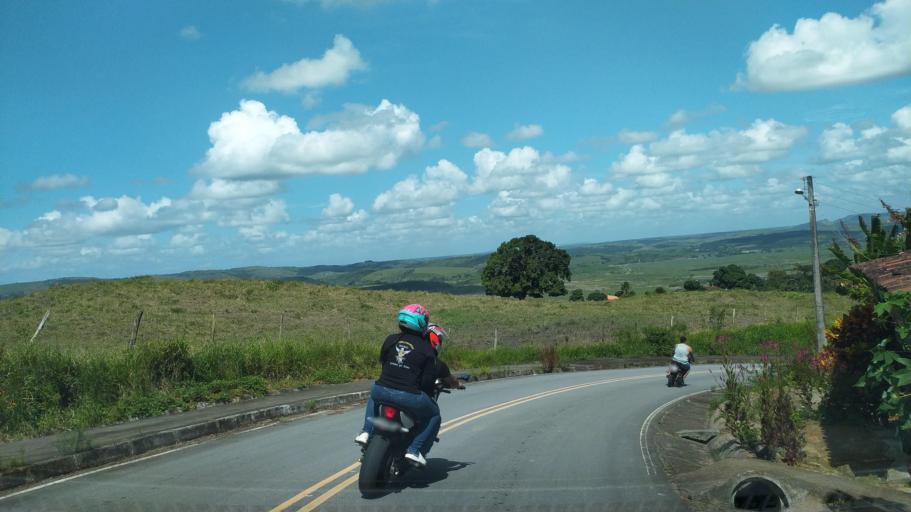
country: BR
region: Alagoas
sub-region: Uniao Dos Palmares
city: Uniao dos Palmares
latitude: -9.1629
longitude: -36.0677
